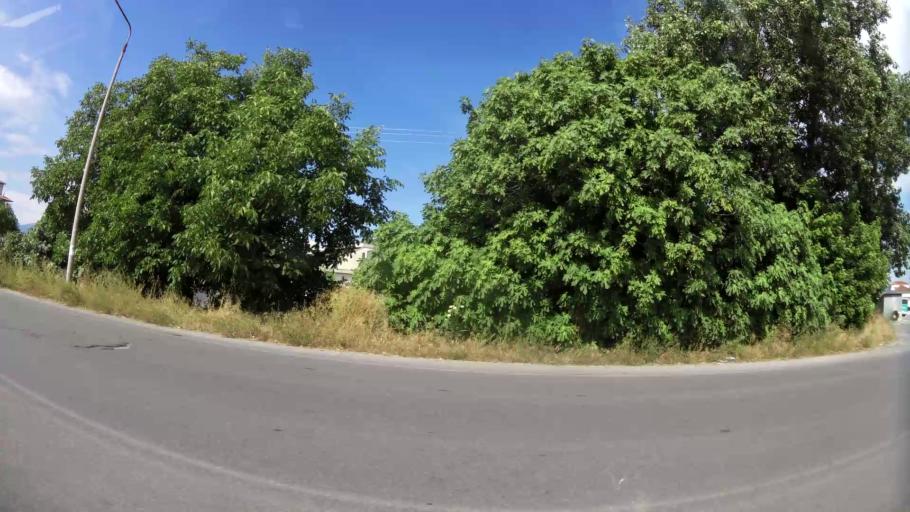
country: GR
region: Central Macedonia
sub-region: Nomos Pierias
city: Katerini
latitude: 40.2791
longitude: 22.5181
